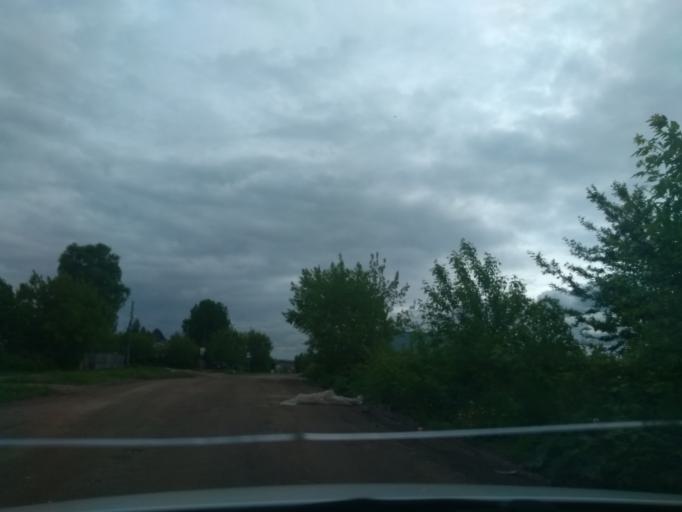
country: RU
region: Perm
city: Froly
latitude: 57.9206
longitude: 56.2687
